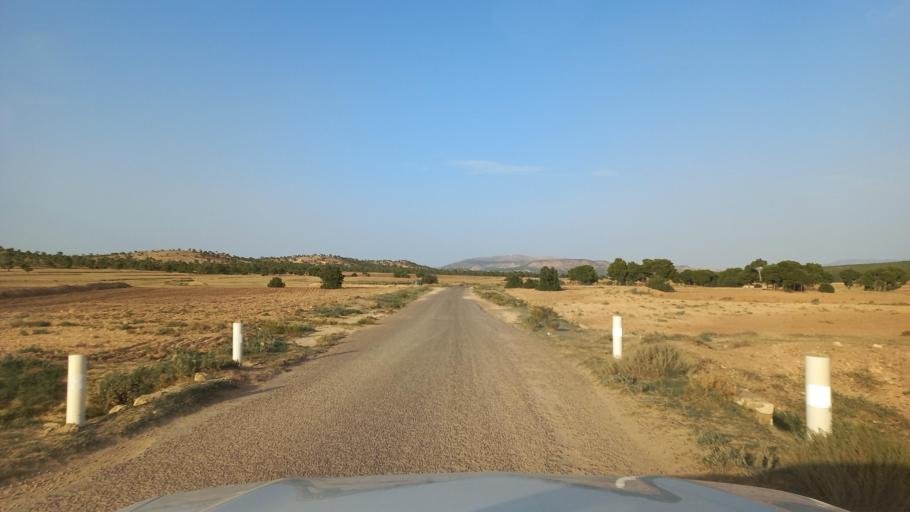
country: TN
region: Al Qasrayn
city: Kasserine
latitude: 35.3933
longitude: 8.8745
